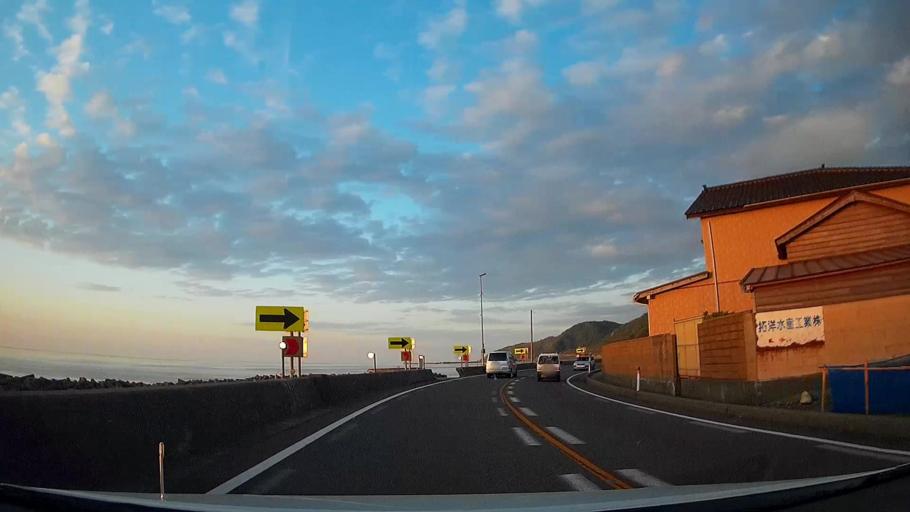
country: JP
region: Niigata
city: Itoigawa
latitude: 37.1202
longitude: 138.0327
